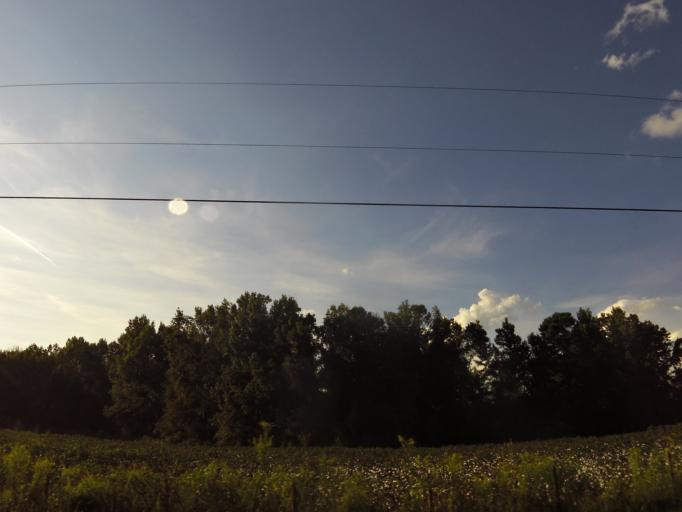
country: US
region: Georgia
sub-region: Lowndes County
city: Remerton
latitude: 30.7925
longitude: -83.3933
